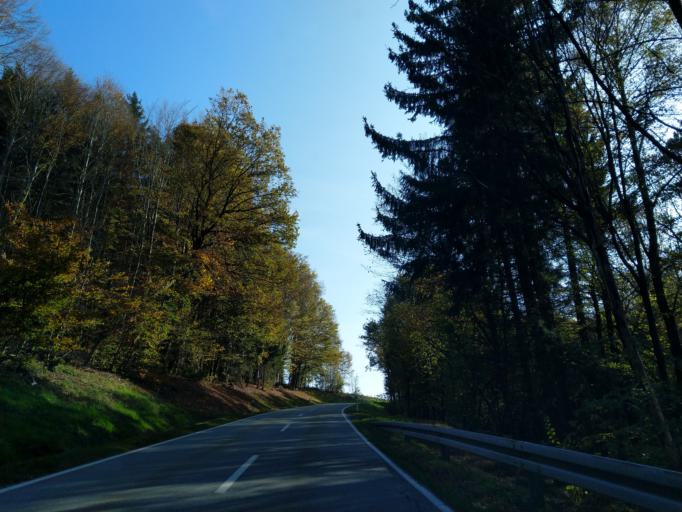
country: DE
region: Bavaria
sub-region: Lower Bavaria
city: Grattersdorf
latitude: 48.8016
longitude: 13.1732
